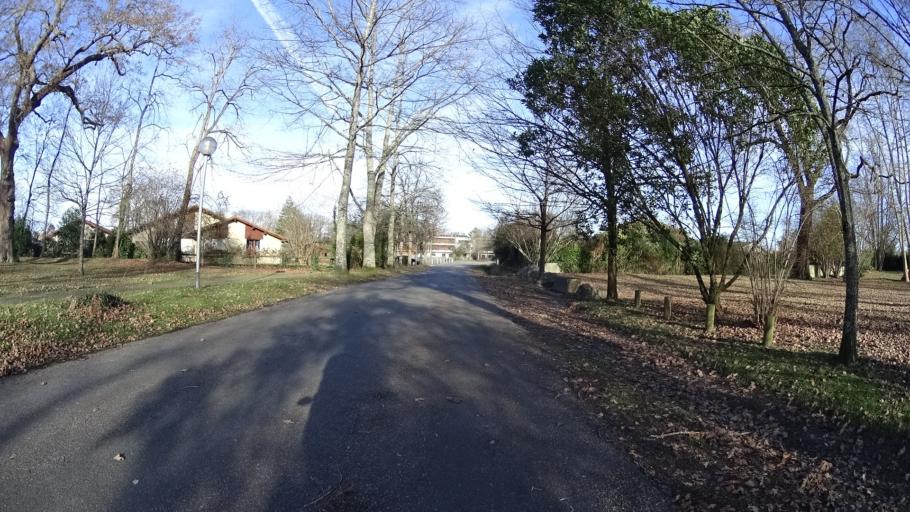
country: FR
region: Aquitaine
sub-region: Departement des Landes
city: Saint-Paul-les-Dax
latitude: 43.7329
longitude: -1.0587
